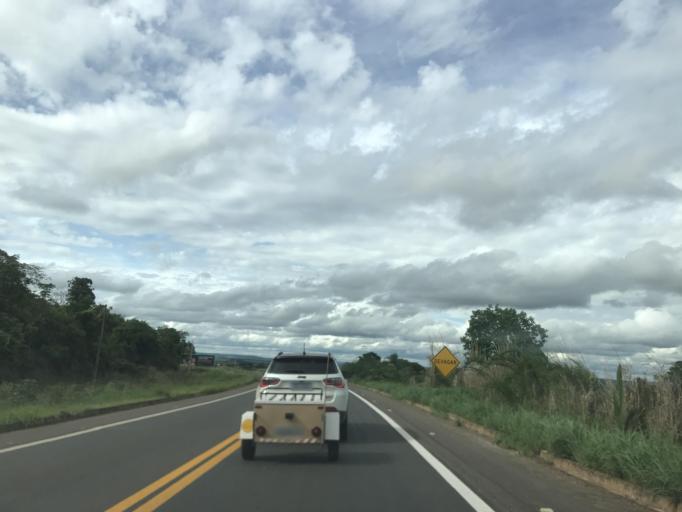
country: BR
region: Goias
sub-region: Piracanjuba
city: Piracanjuba
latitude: -17.2111
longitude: -48.7079
